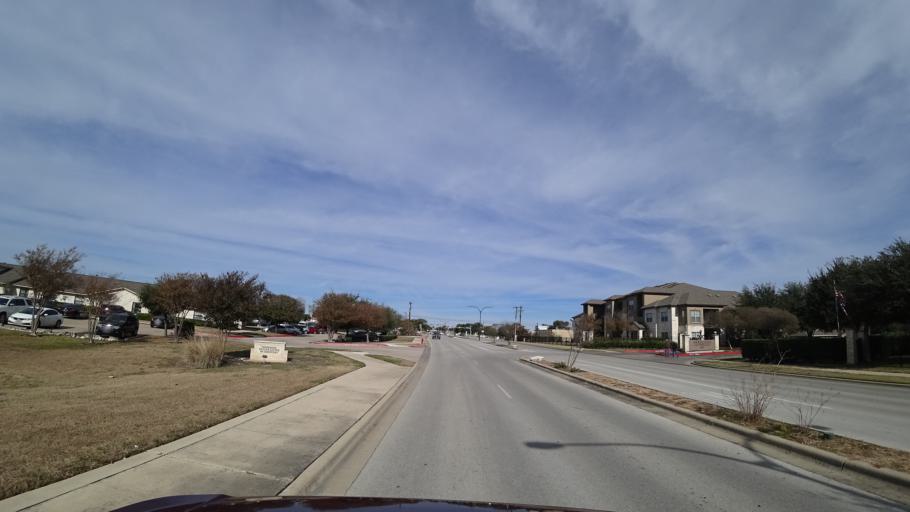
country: US
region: Texas
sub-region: Williamson County
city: Cedar Park
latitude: 30.5220
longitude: -97.8200
